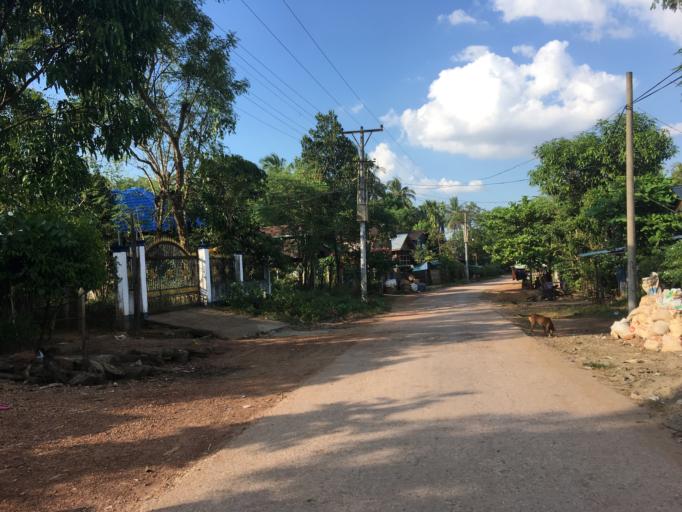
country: MM
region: Mon
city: Mawlamyine
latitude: 16.4370
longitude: 97.6205
